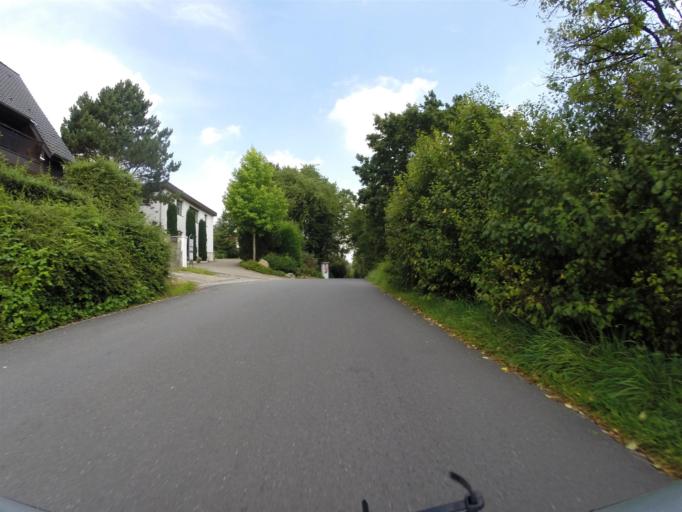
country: DE
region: North Rhine-Westphalia
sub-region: Regierungsbezirk Detmold
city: Herford
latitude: 52.1374
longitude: 8.6675
